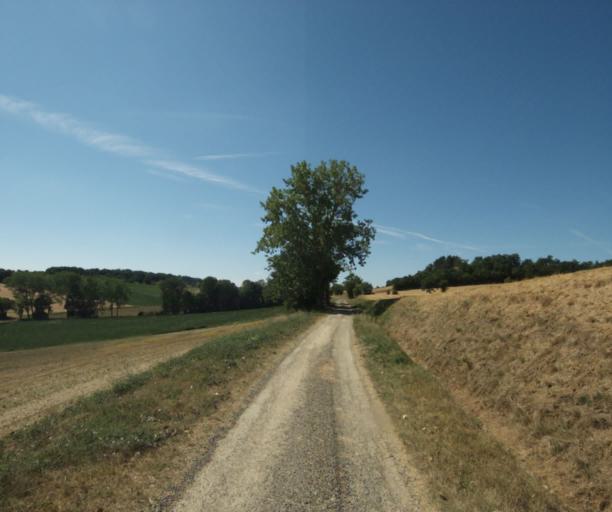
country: FR
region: Midi-Pyrenees
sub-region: Departement de la Haute-Garonne
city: Saint-Felix-Lauragais
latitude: 43.4981
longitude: 1.9341
